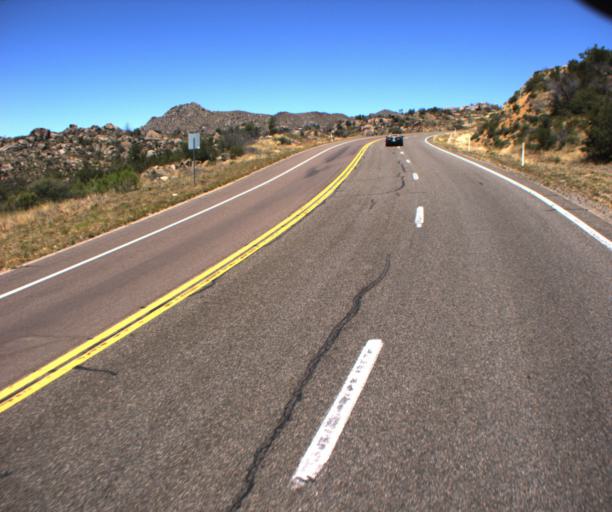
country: US
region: Arizona
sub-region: Yavapai County
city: Congress
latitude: 34.2083
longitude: -112.7538
